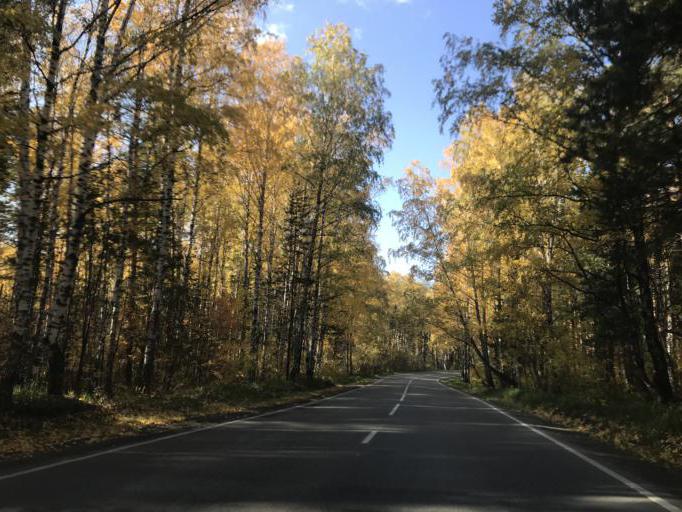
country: RU
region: Chelyabinsk
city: Dolgoderevenskoye
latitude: 55.2833
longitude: 61.3614
